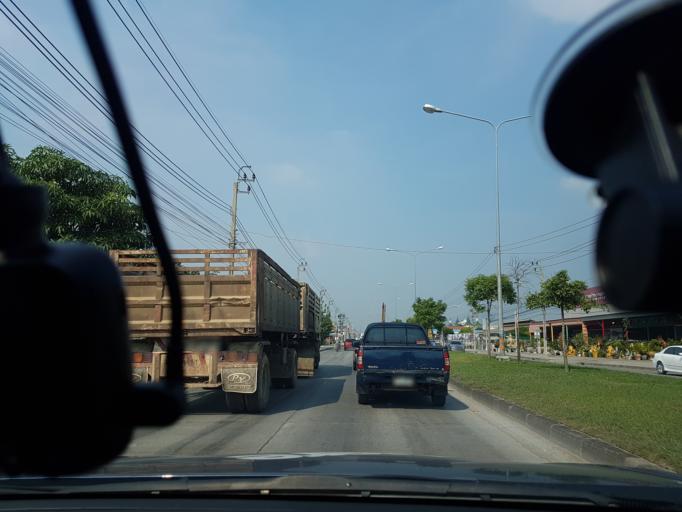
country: TH
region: Bangkok
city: Khlong Sam Wa
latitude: 13.8433
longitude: 100.7206
